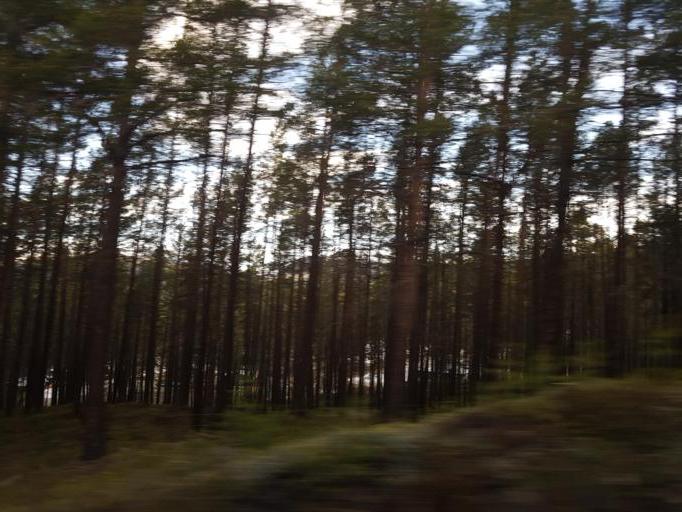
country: NO
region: Oppland
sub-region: Dovre
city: Dombas
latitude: 62.0843
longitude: 9.1393
